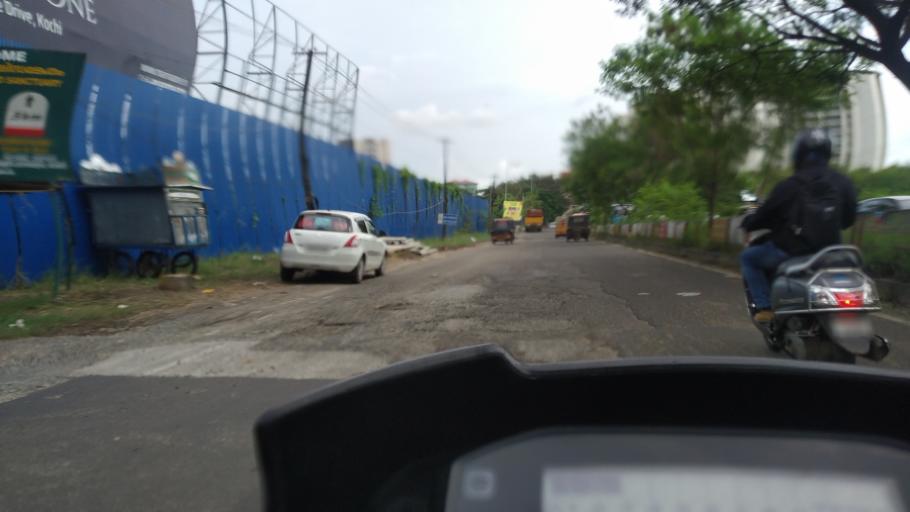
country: IN
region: Kerala
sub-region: Ernakulam
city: Cochin
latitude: 9.9929
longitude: 76.2703
